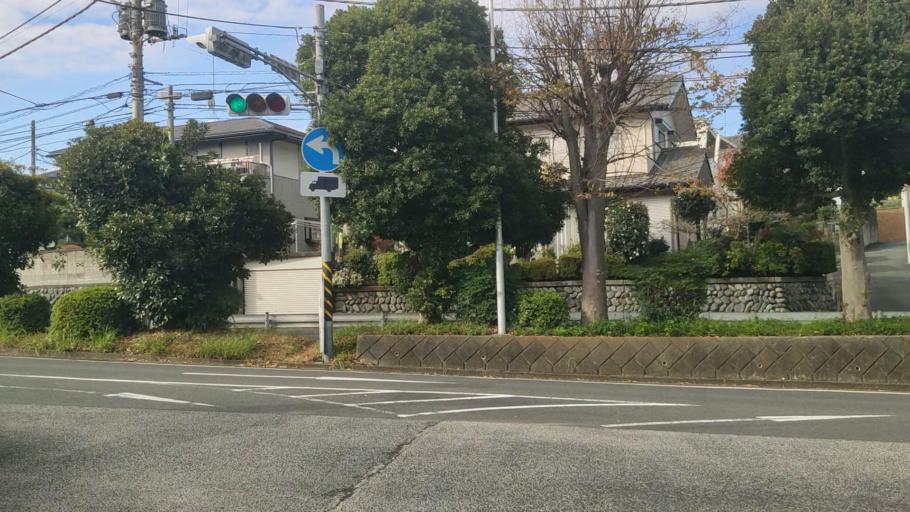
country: JP
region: Kanagawa
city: Minami-rinkan
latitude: 35.4535
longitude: 139.5369
